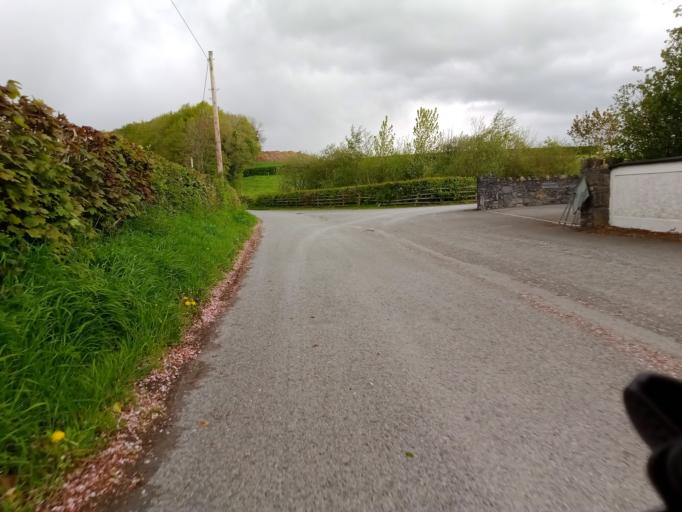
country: IE
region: Leinster
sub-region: Kilkenny
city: Kilkenny
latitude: 52.6837
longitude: -7.2678
